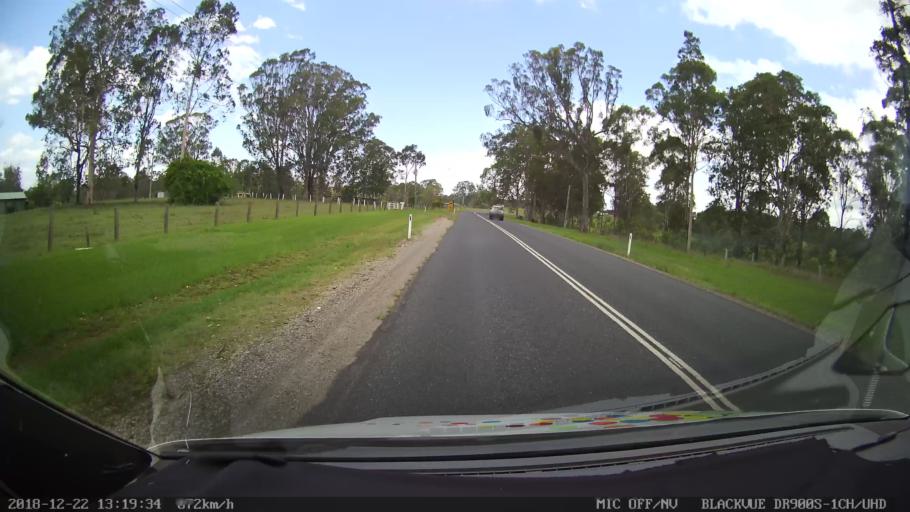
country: AU
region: New South Wales
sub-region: Clarence Valley
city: South Grafton
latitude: -29.7577
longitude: 152.9293
